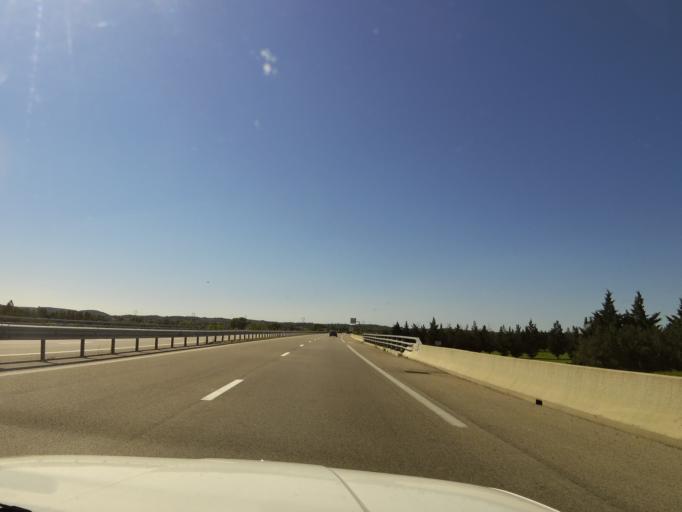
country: FR
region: Languedoc-Roussillon
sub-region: Departement du Gard
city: La Calmette
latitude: 43.9382
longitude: 4.2539
